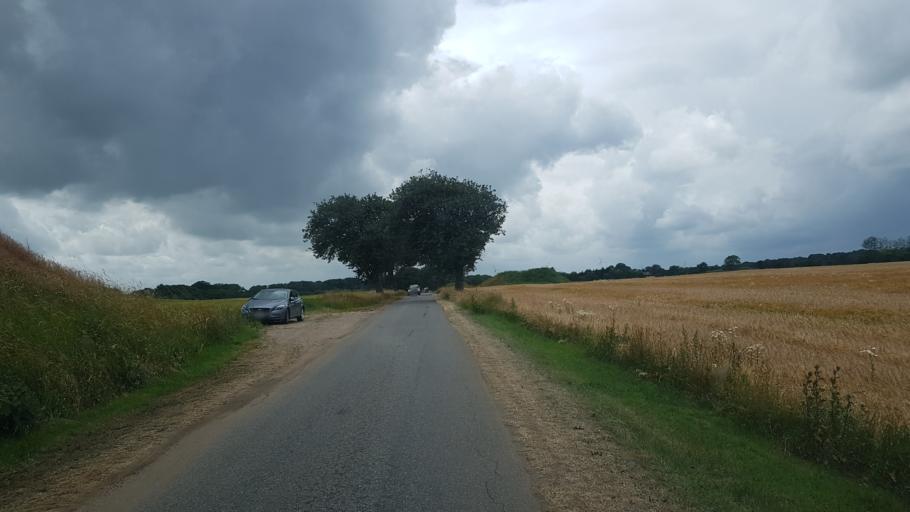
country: DK
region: South Denmark
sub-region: Kolding Kommune
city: Lunderskov
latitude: 55.5046
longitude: 9.3171
